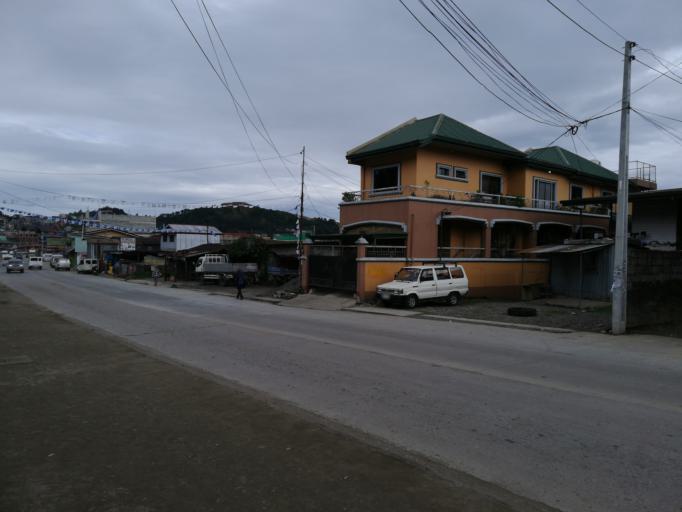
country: PH
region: Cordillera
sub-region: Province of Benguet
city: La Trinidad
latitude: 16.4485
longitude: 120.5762
